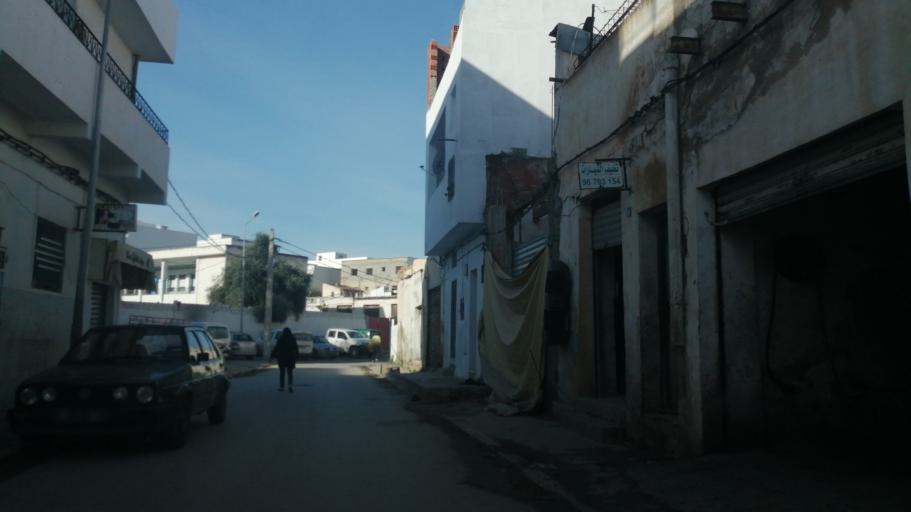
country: TN
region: Tunis
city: Tunis
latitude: 36.8117
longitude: 10.1740
